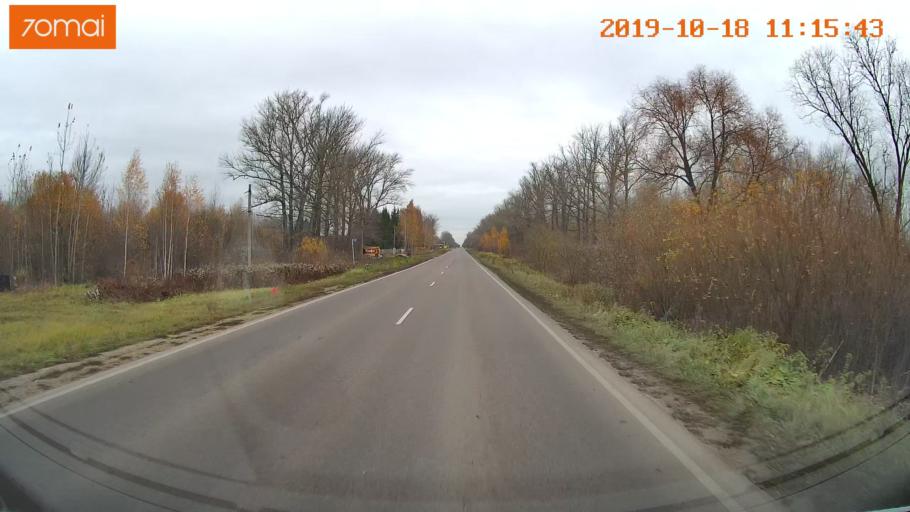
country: RU
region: Tula
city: Kimovsk
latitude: 53.9962
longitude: 38.5478
